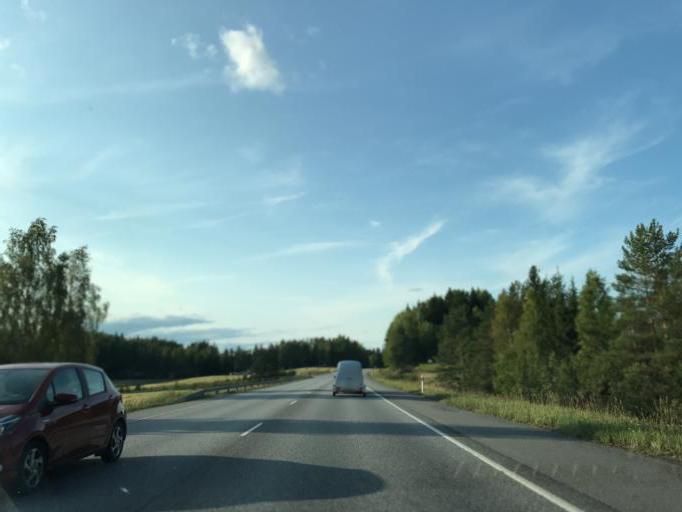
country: FI
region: Uusimaa
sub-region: Helsinki
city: Vihti
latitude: 60.3644
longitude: 24.3202
